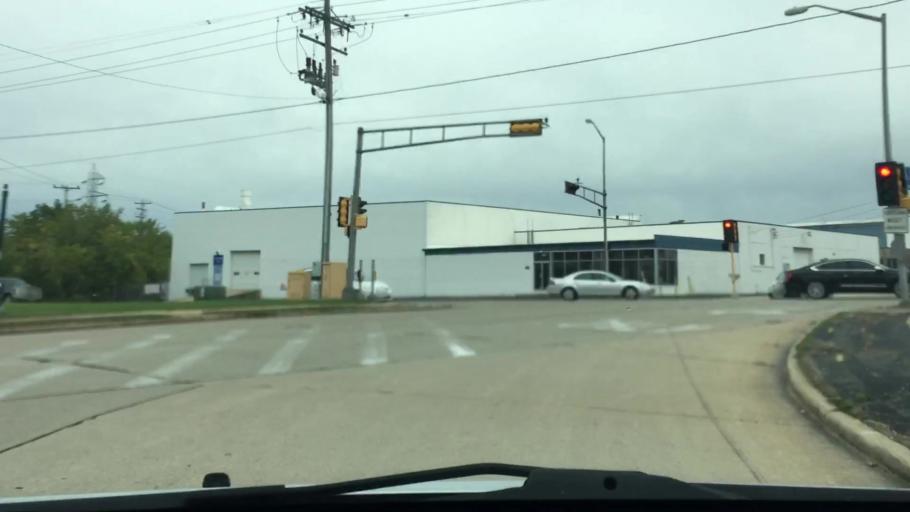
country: US
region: Wisconsin
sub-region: Waukesha County
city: Waukesha
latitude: 43.0183
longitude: -88.2140
